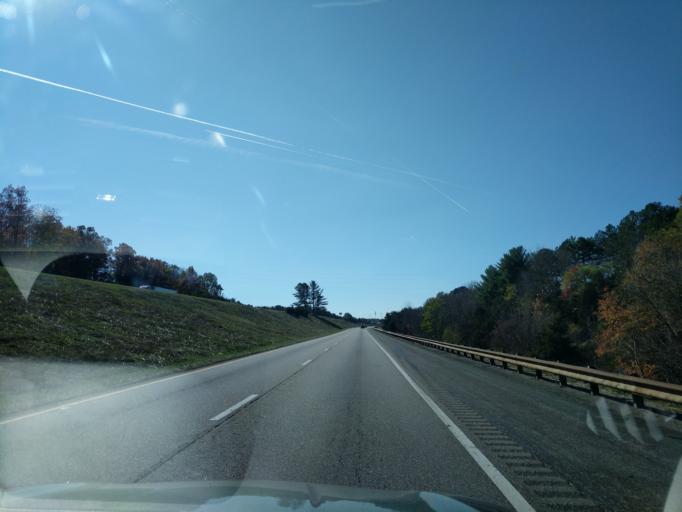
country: US
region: Virginia
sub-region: City of Staunton
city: Staunton
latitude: 38.1389
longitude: -79.0238
